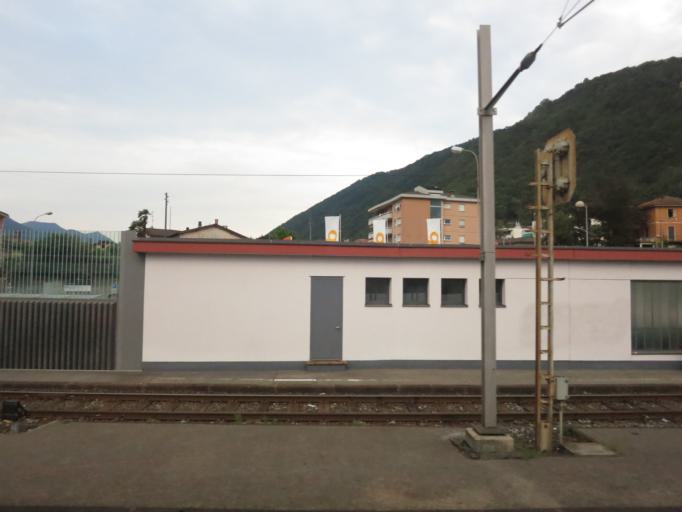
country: CH
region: Ticino
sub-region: Lugano District
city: Melide
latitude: 45.9557
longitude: 8.9488
